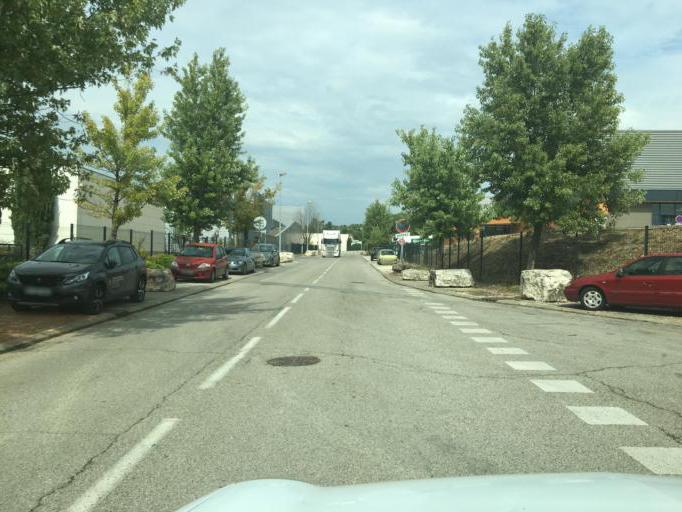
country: FR
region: Provence-Alpes-Cote d'Azur
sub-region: Departement des Bouches-du-Rhone
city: Bouc-Bel-Air
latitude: 43.4858
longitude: 5.3862
